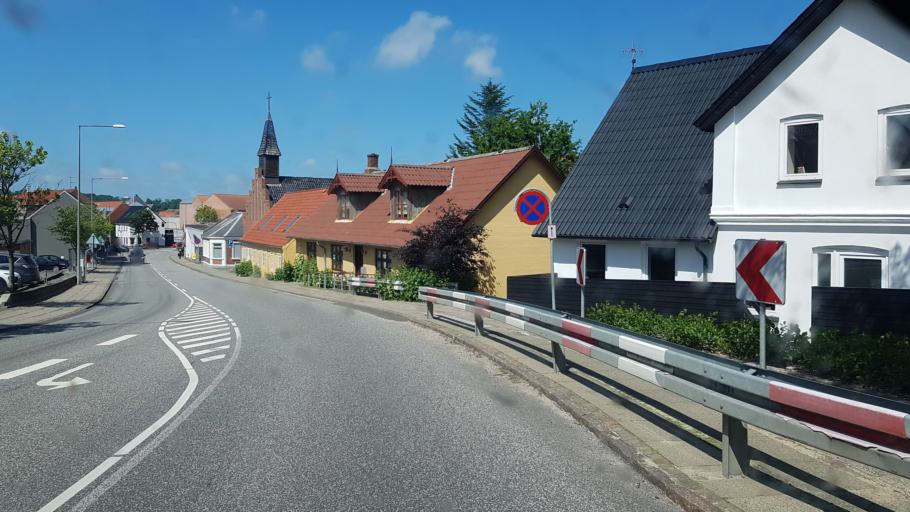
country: DK
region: Central Jutland
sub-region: Lemvig Kommune
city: Lemvig
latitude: 56.5500
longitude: 8.3155
